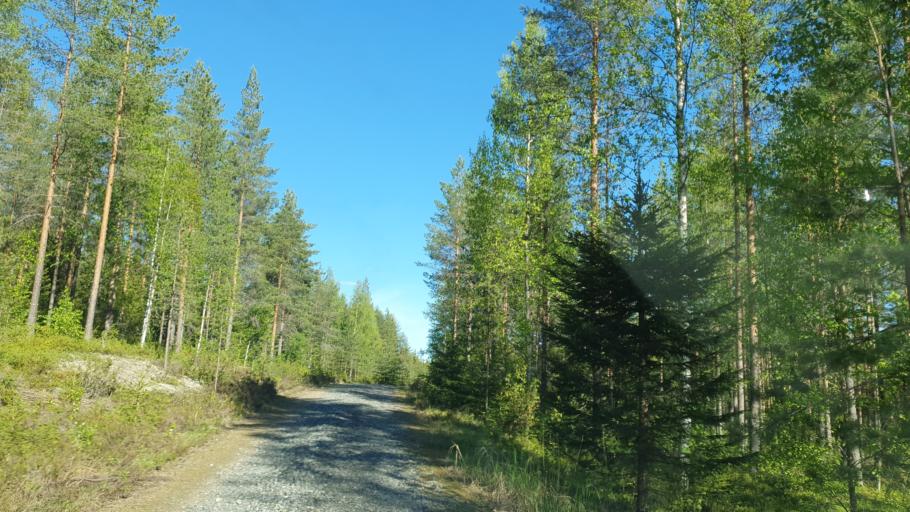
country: FI
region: Kainuu
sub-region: Kehys-Kainuu
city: Kuhmo
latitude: 64.1802
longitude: 29.4143
